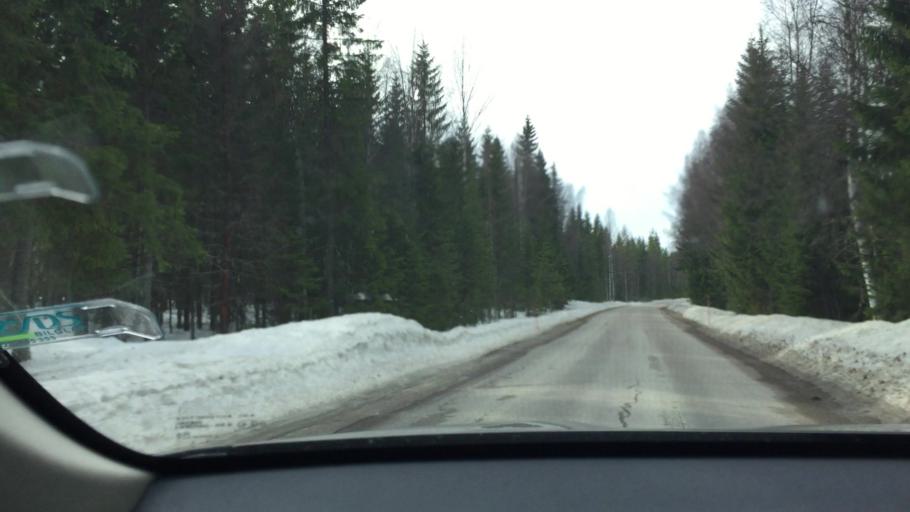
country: NO
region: Hedmark
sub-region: Trysil
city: Innbygda
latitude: 61.0677
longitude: 12.5414
